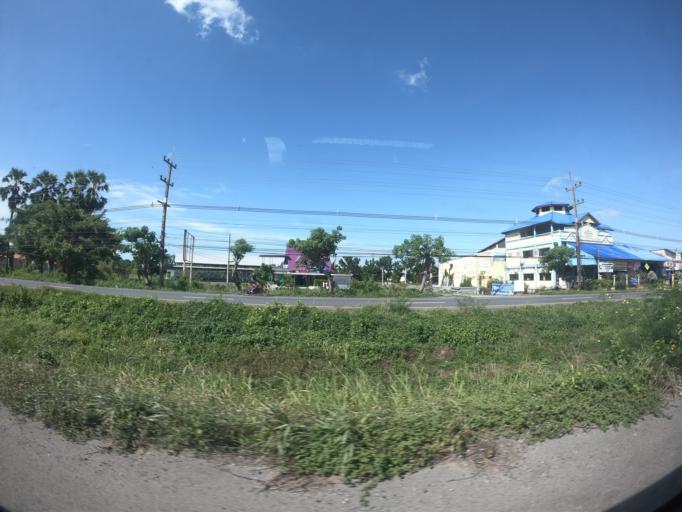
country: TH
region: Nakhon Nayok
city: Ban Na
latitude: 14.2486
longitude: 101.1037
